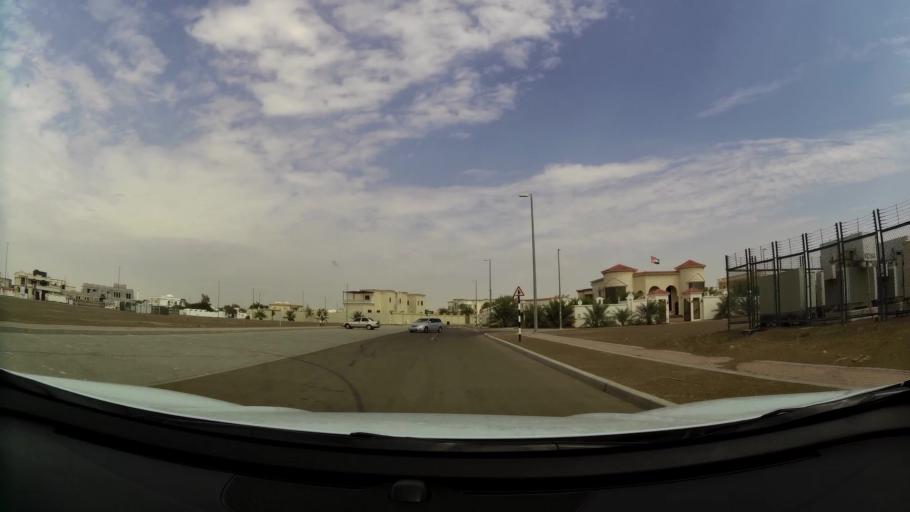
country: AE
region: Abu Dhabi
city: Al Ain
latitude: 24.1976
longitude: 55.8025
